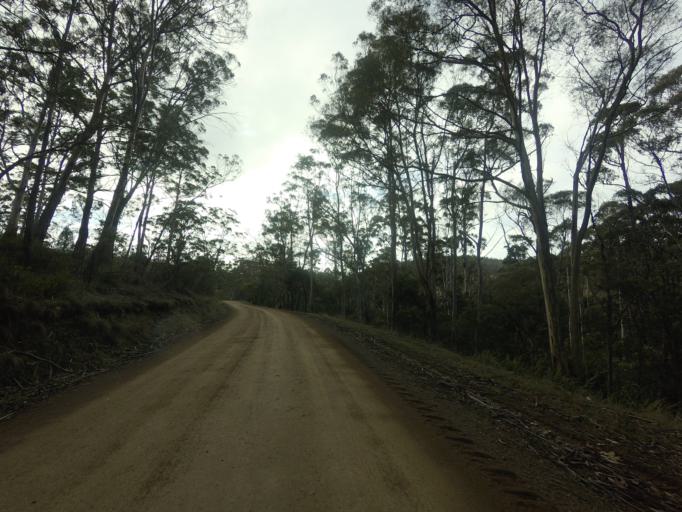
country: AU
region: Tasmania
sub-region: Derwent Valley
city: New Norfolk
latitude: -42.7515
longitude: 146.8759
